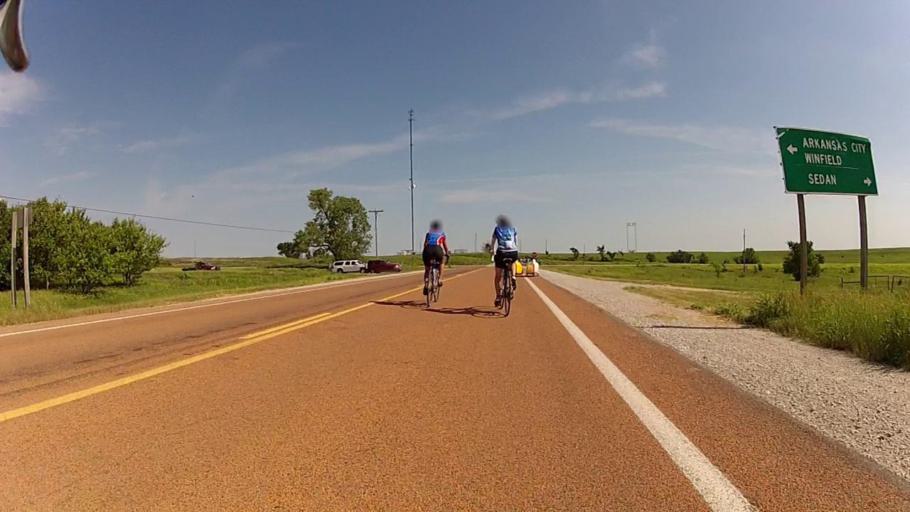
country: US
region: Kansas
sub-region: Cowley County
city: Winfield
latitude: 37.1095
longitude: -96.6436
